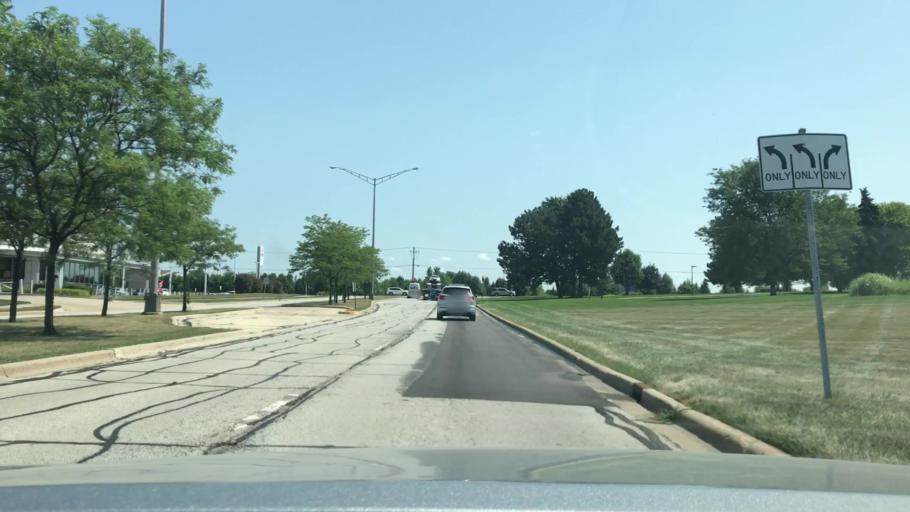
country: US
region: Illinois
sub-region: DuPage County
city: Naperville
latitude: 41.7513
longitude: -88.2183
